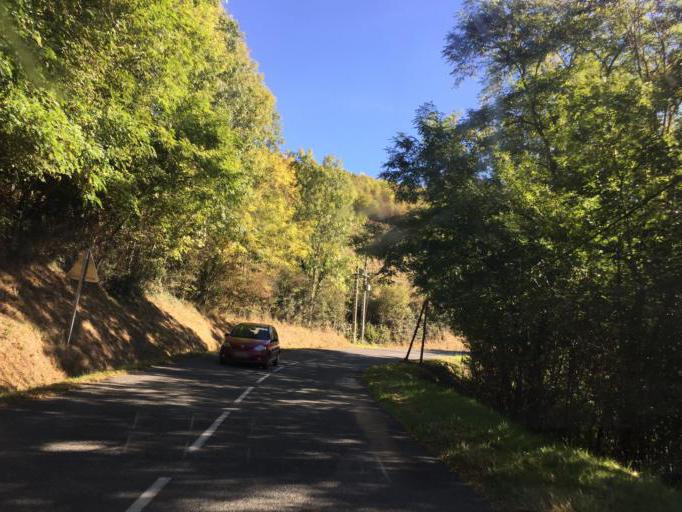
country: FR
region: Rhone-Alpes
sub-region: Departement du Rhone
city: Grandris
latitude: 46.0304
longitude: 4.5297
